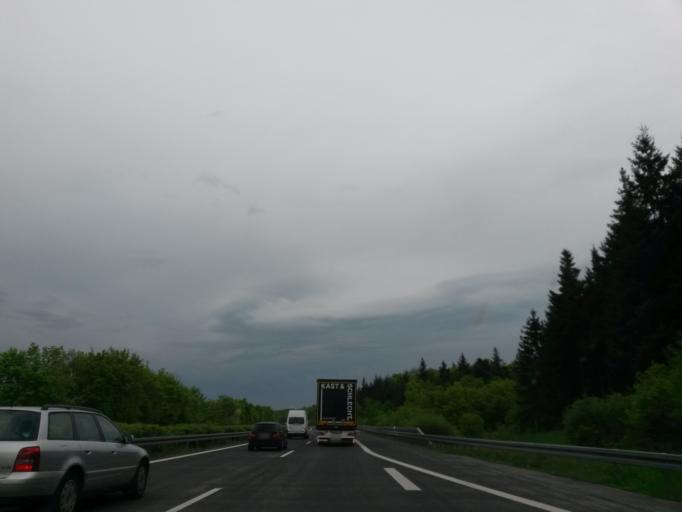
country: DE
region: Baden-Wuerttemberg
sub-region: Regierungsbezirk Stuttgart
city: Buch am Ahorn
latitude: 49.4799
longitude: 9.5654
